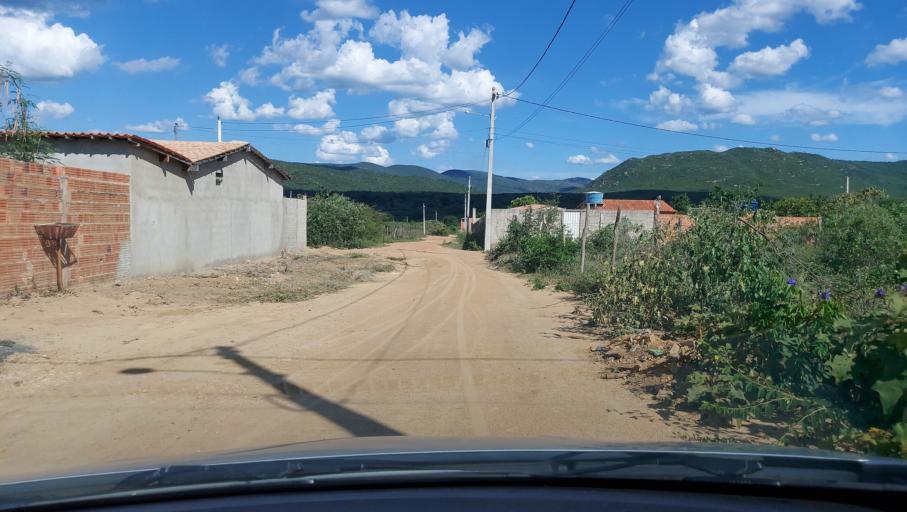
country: BR
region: Bahia
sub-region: Oliveira Dos Brejinhos
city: Beira Rio
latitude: -12.0068
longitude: -42.6327
